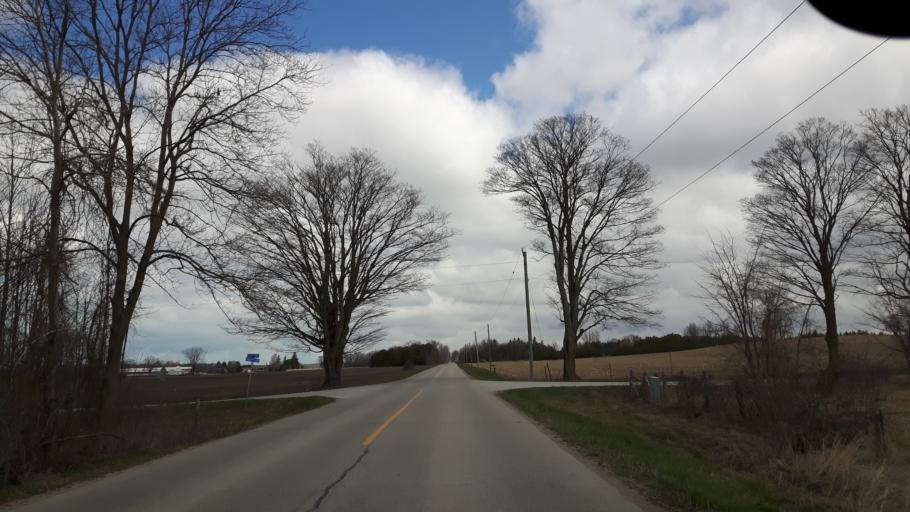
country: CA
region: Ontario
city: Goderich
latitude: 43.6793
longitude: -81.6846
